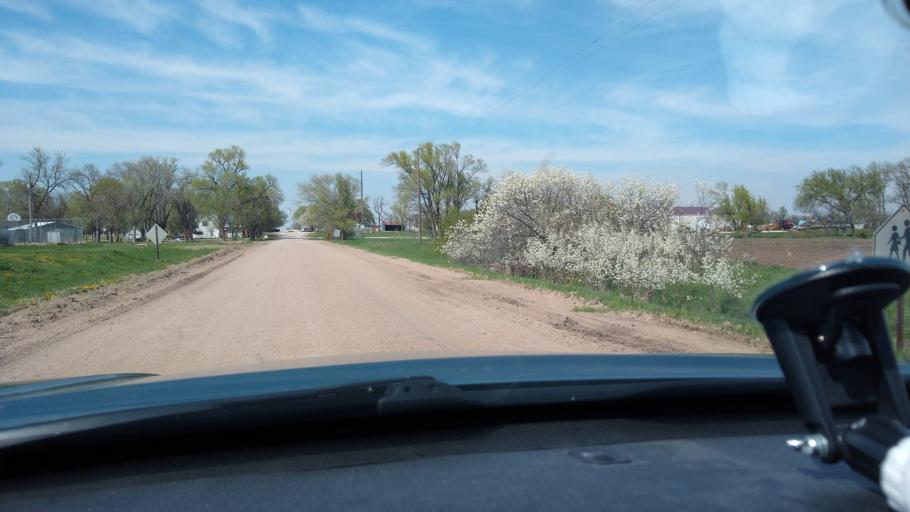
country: US
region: Nebraska
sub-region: Fillmore County
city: Geneva
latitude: 40.4115
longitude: -97.5868
